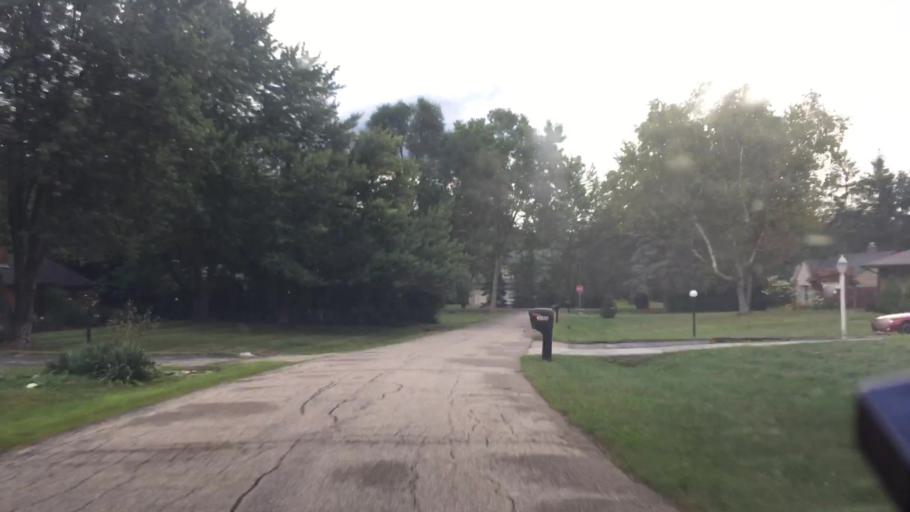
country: US
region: Michigan
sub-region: Oakland County
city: Bloomfield Hills
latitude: 42.5831
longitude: -83.2780
